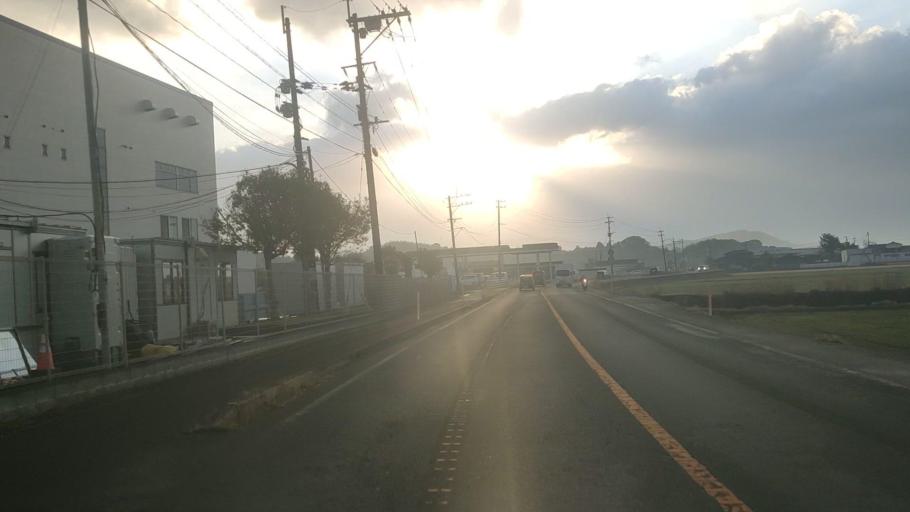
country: JP
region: Kumamoto
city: Uto
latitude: 32.7266
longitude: 130.7645
